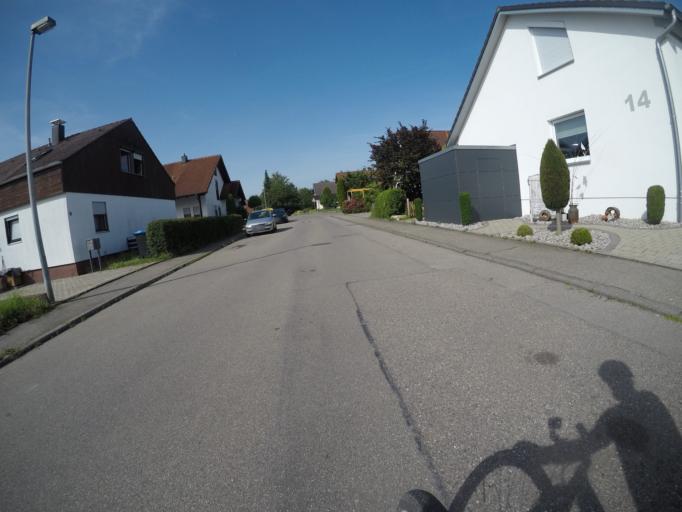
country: DE
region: Baden-Wuerttemberg
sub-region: Regierungsbezirk Stuttgart
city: Herrenberg
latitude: 48.6128
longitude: 8.8460
